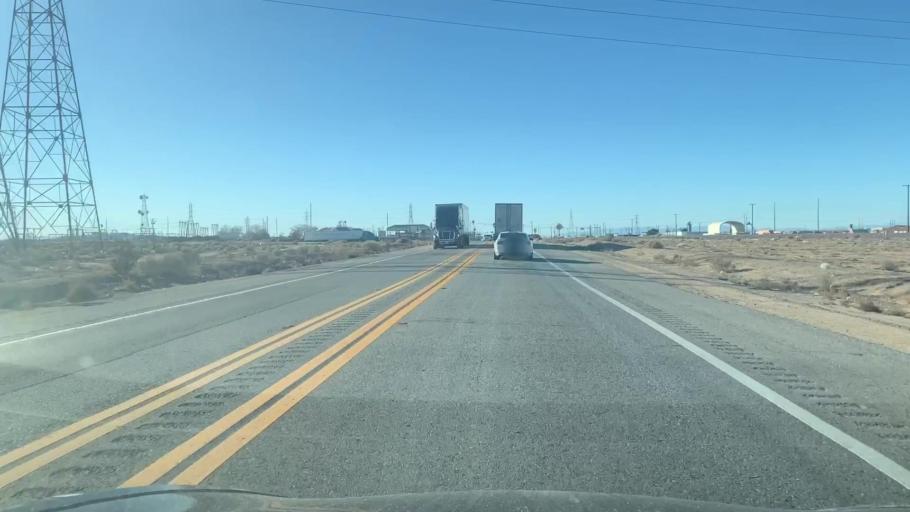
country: US
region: California
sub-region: Kern County
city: Boron
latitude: 34.9917
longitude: -117.5340
